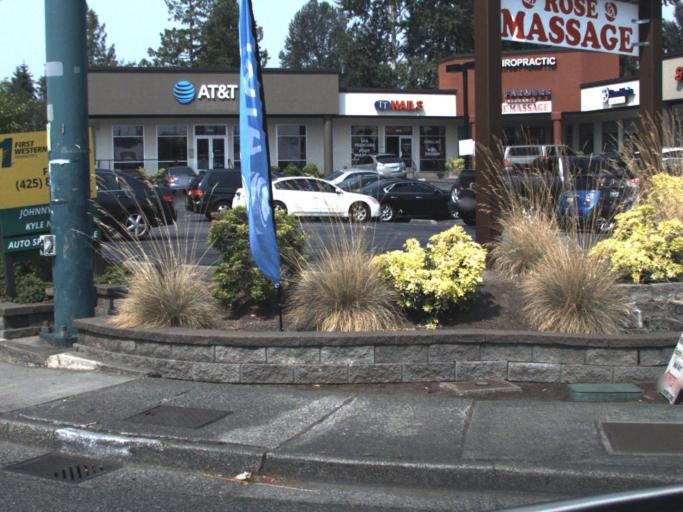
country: US
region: Washington
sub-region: Snohomish County
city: Mill Creek
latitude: 47.9083
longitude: -122.2283
